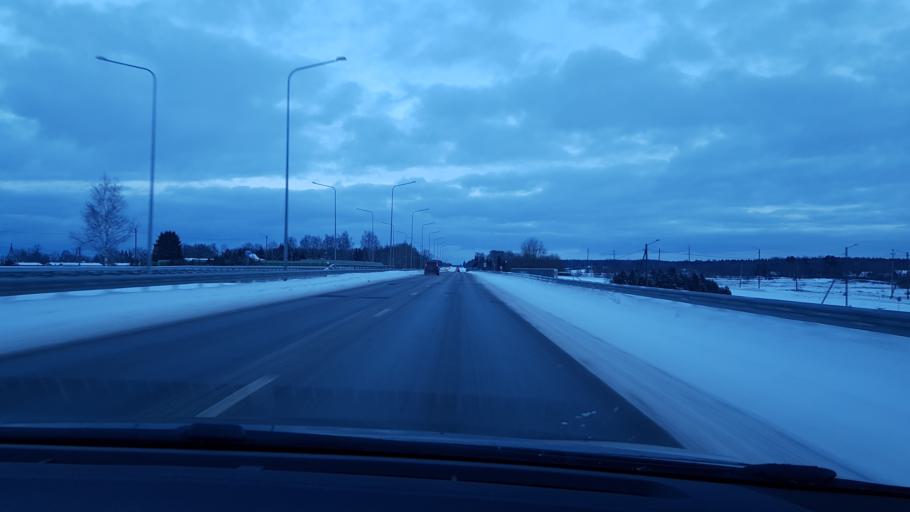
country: EE
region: Harju
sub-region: Kuusalu vald
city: Kuusalu
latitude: 59.4451
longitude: 25.3753
